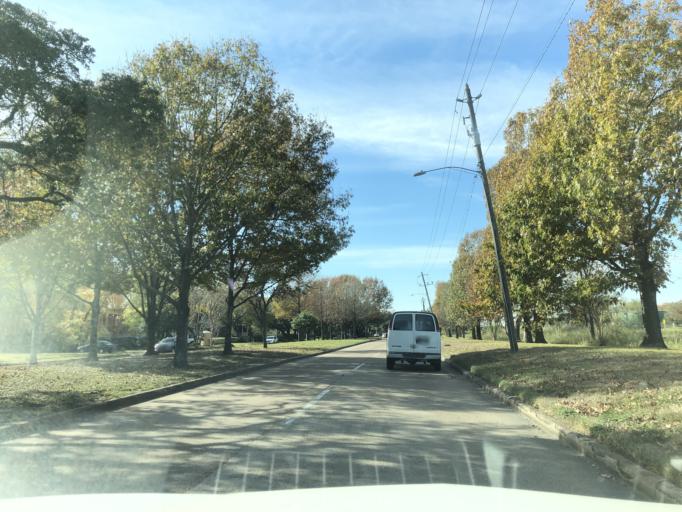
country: US
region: Texas
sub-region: Harris County
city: Bellaire
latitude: 29.6788
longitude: -95.4652
